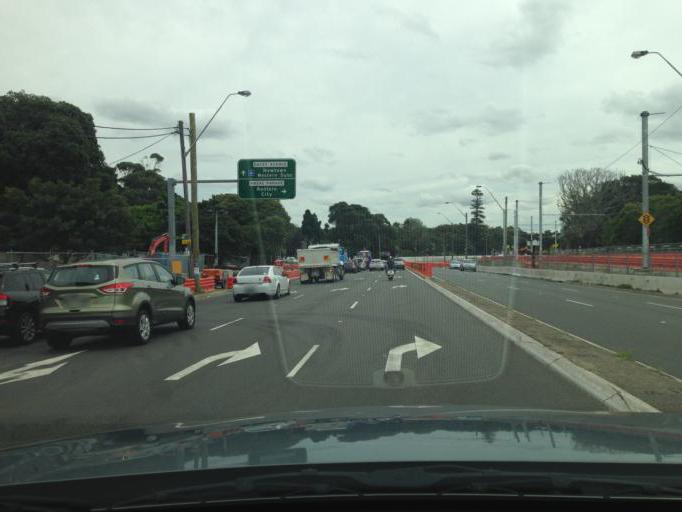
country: AU
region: New South Wales
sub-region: Randwick
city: Kensington
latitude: -33.9025
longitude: 151.2239
